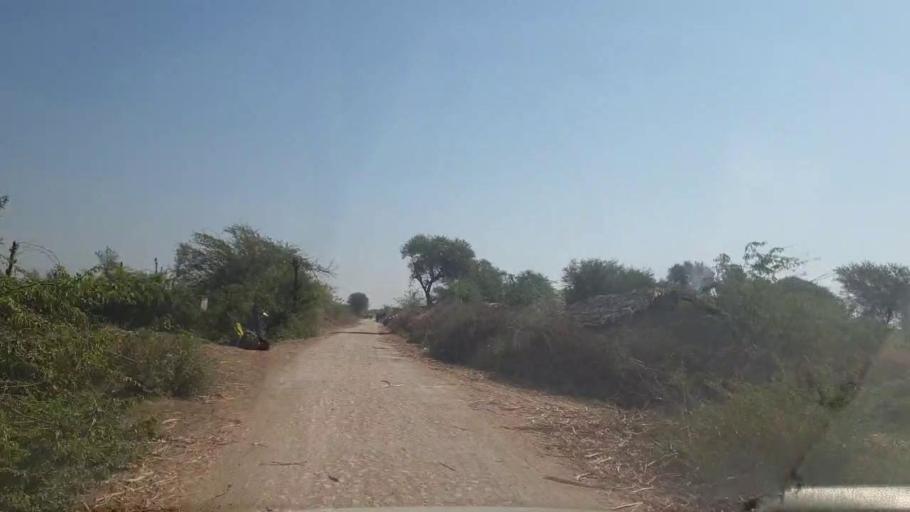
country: PK
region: Sindh
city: Mirpur Khas
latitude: 25.5440
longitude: 69.1917
